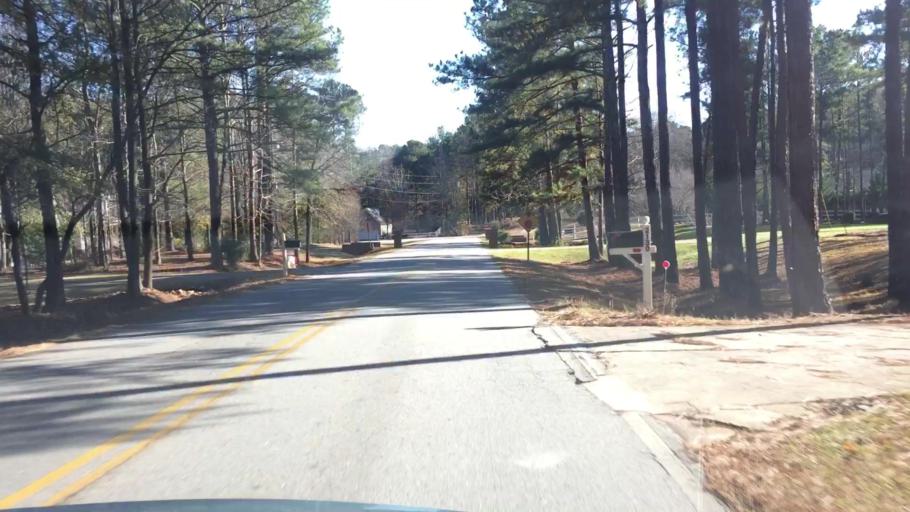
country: US
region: Georgia
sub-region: Henry County
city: McDonough
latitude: 33.4970
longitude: -84.0715
